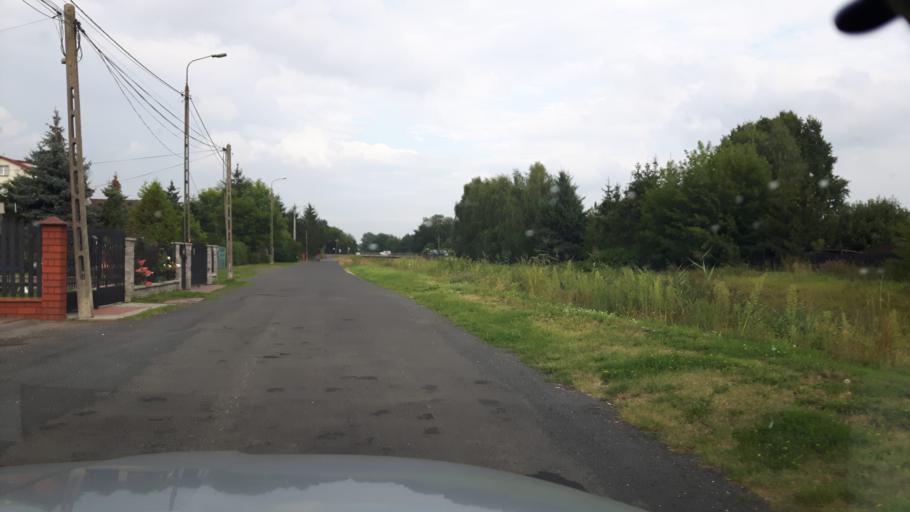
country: PL
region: Masovian Voivodeship
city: Zielonka
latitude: 52.3129
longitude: 21.1360
